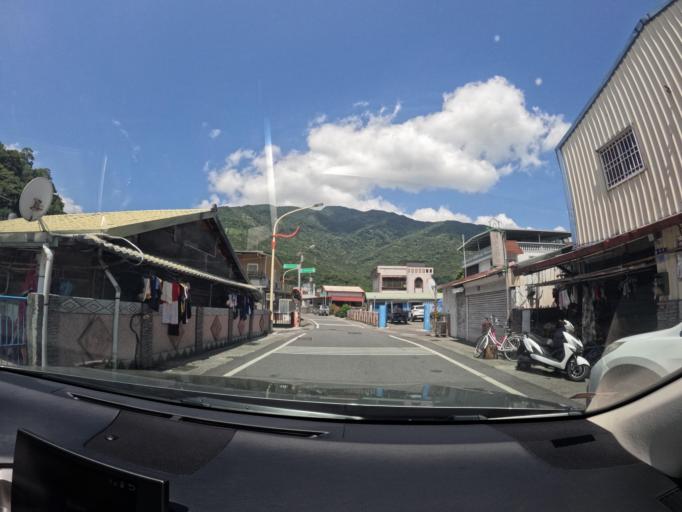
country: TW
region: Taiwan
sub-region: Hualien
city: Hualian
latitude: 23.7162
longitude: 121.4095
